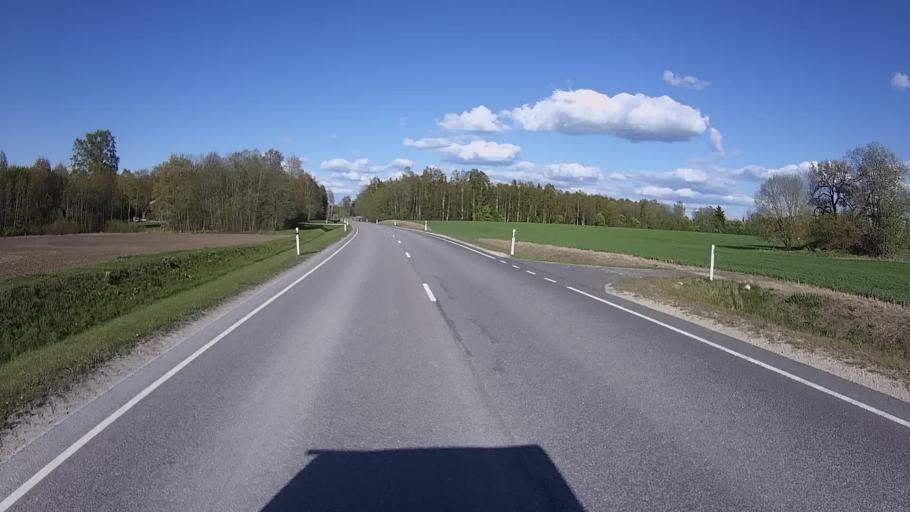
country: EE
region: Jogevamaa
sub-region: Poltsamaa linn
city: Poltsamaa
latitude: 58.6314
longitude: 25.7914
